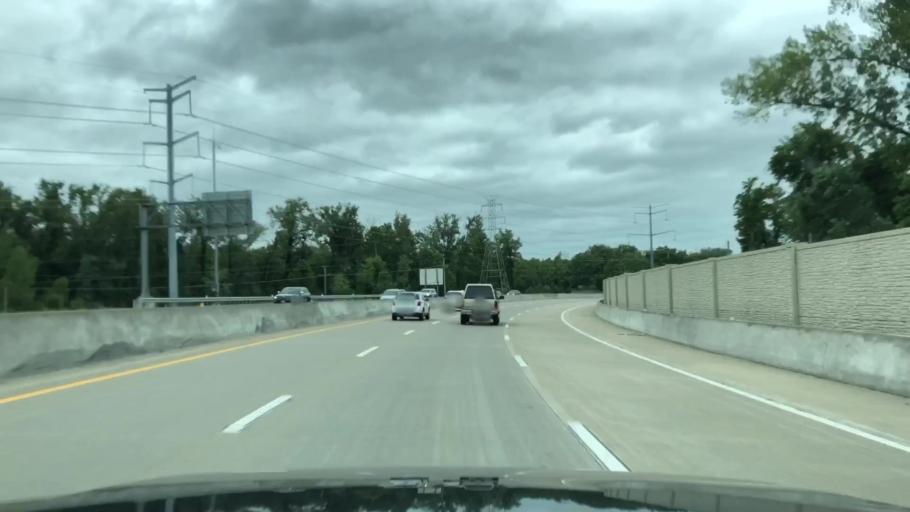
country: US
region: Missouri
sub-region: Saint Louis County
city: Town and Country
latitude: 38.6721
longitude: -90.4942
